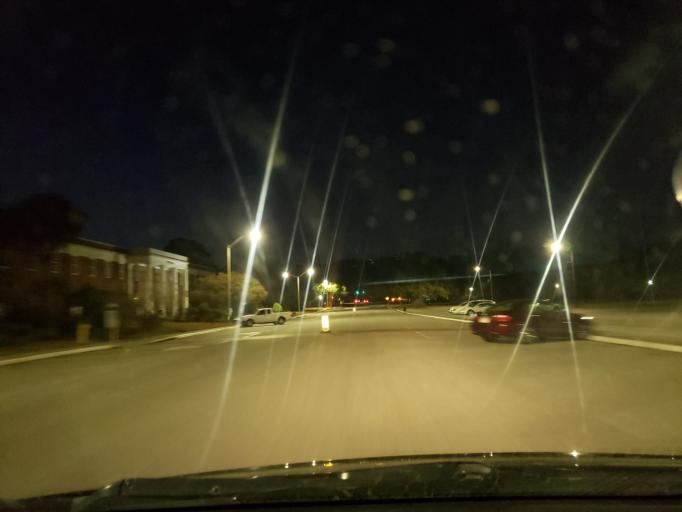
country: US
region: Georgia
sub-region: Chatham County
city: Montgomery
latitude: 31.9803
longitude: -81.1605
